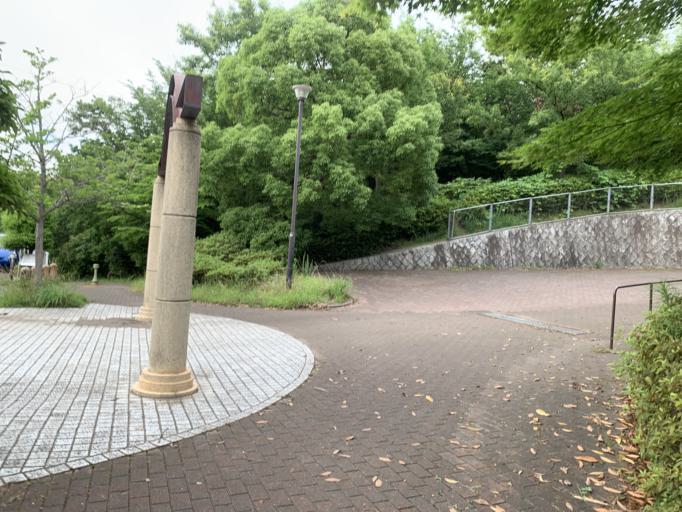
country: JP
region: Kanagawa
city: Yokohama
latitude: 35.5471
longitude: 139.5982
